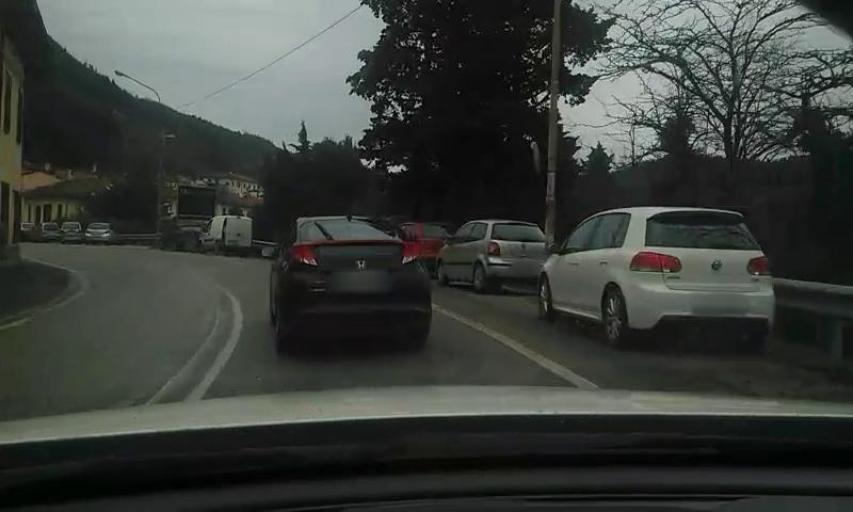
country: IT
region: Tuscany
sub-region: Provincia di Prato
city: Vaiano
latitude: 43.9345
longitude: 11.1263
